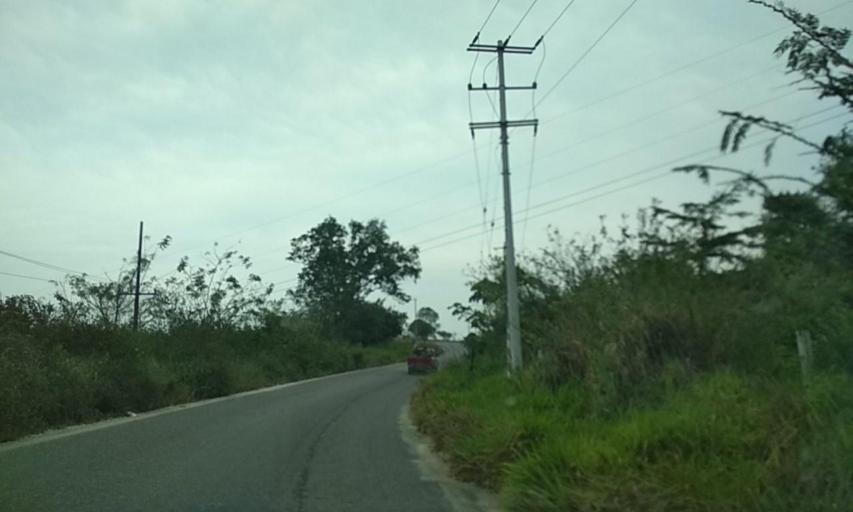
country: MX
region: Veracruz
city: Las Choapas
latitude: 17.8523
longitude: -94.1055
